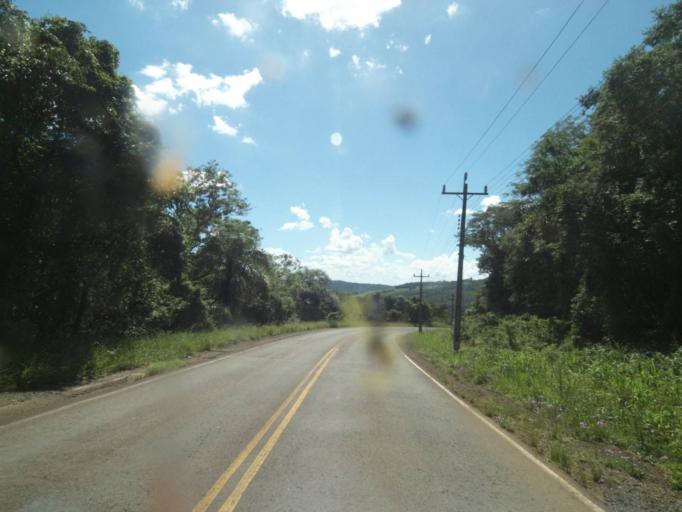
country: BR
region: Parana
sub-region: Chopinzinho
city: Chopinzinho
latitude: -25.7778
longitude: -52.1105
